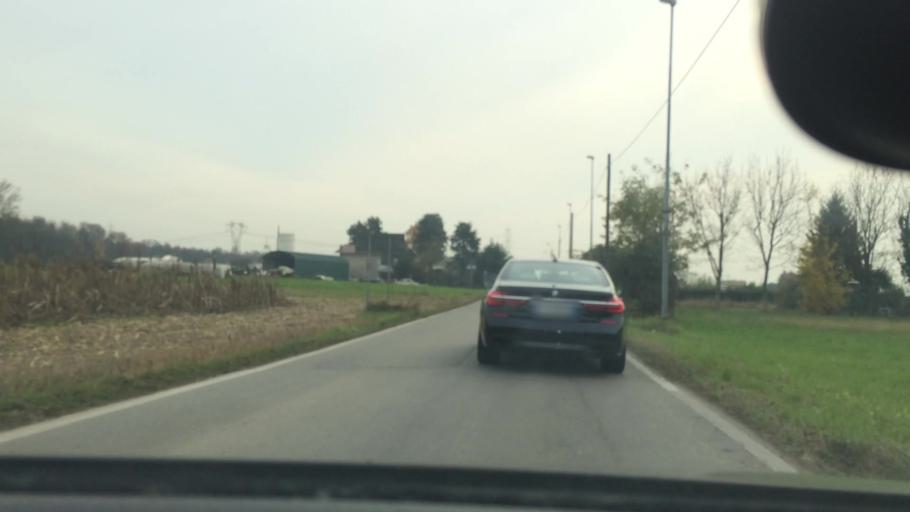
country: IT
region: Lombardy
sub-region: Provincia di Monza e Brianza
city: Misinto
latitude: 45.6567
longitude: 9.0818
